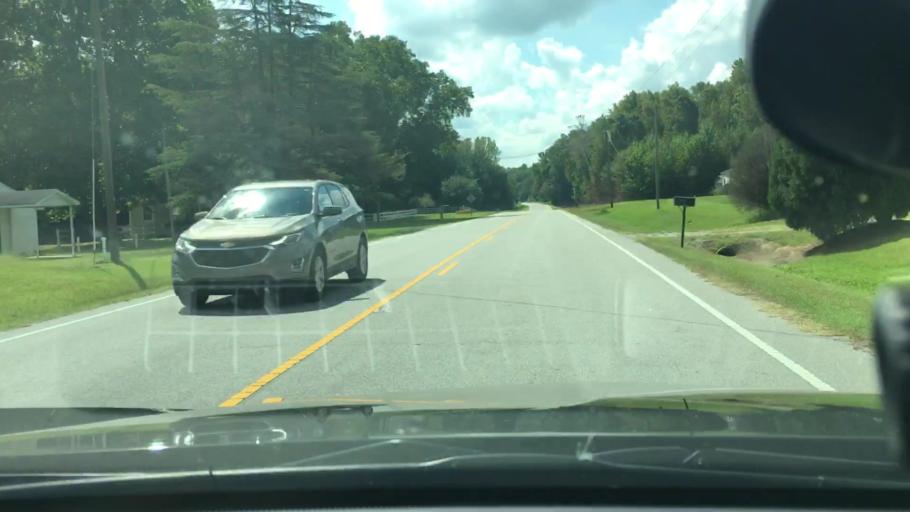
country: US
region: North Carolina
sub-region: Edgecombe County
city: Pinetops
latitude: 35.7273
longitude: -77.5315
